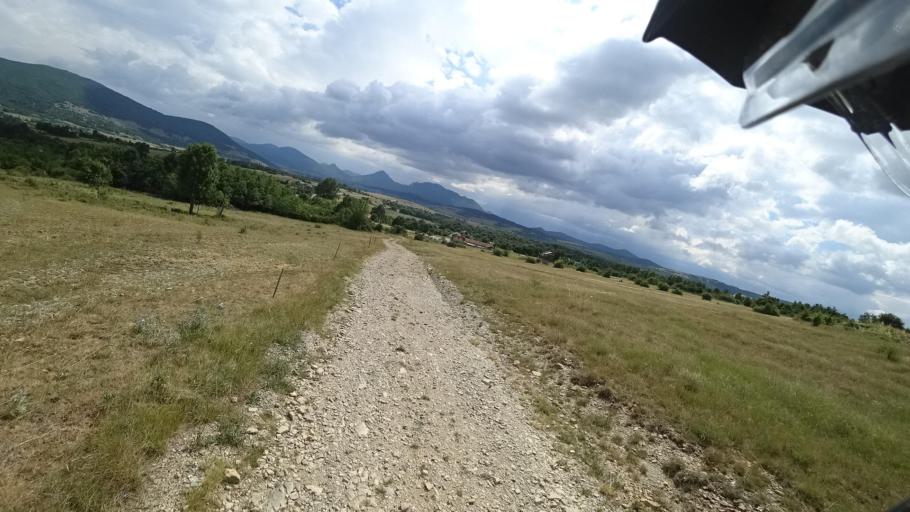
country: HR
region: Zadarska
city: Gracac
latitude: 44.5263
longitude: 15.7650
